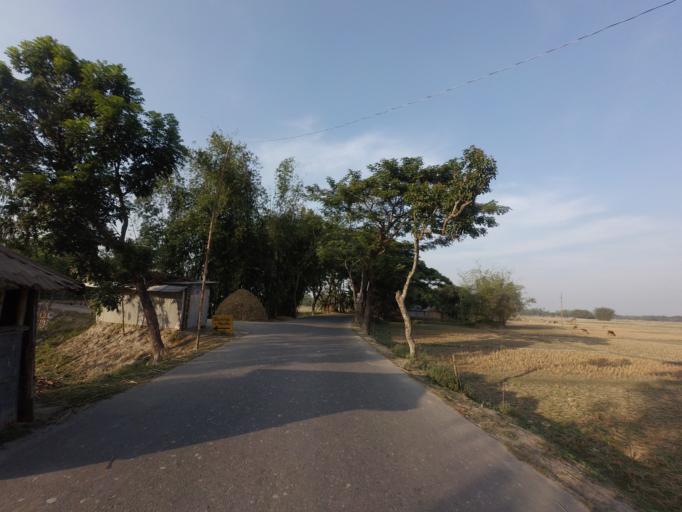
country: BD
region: Rajshahi
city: Saidpur
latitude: 26.0037
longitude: 88.7580
